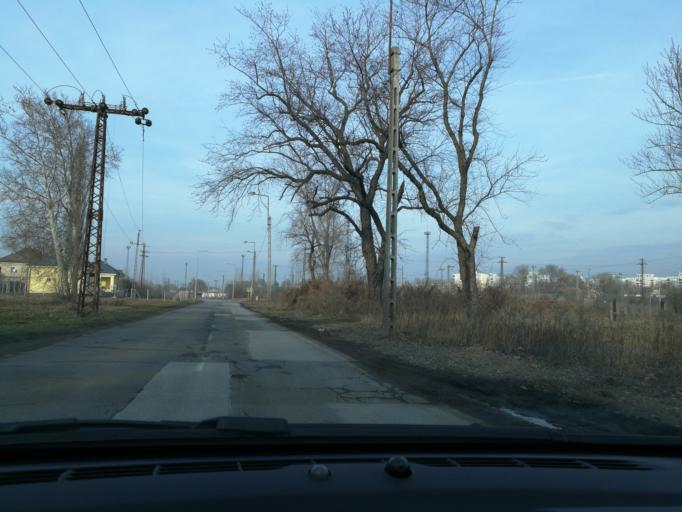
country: HU
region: Szabolcs-Szatmar-Bereg
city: Nyiregyhaza
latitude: 47.9391
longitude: 21.7077
